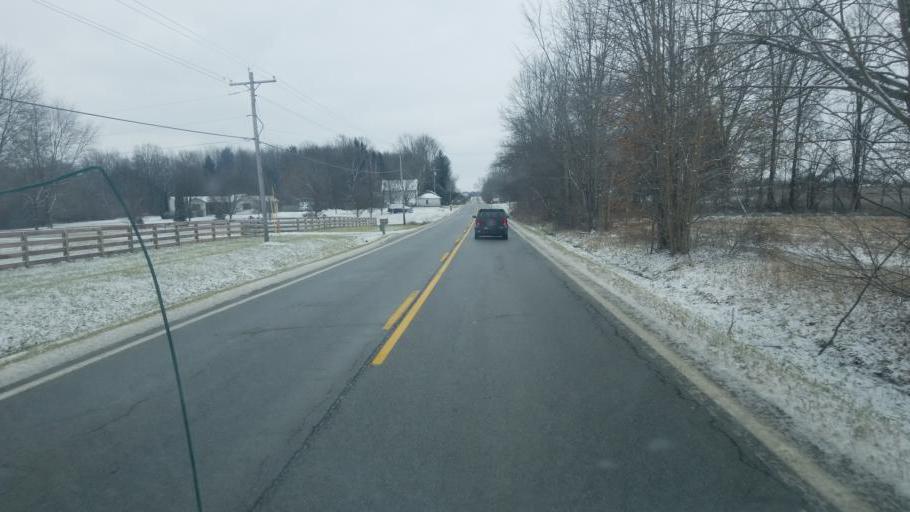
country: US
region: Ohio
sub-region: Licking County
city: Johnstown
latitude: 40.1995
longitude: -82.7702
